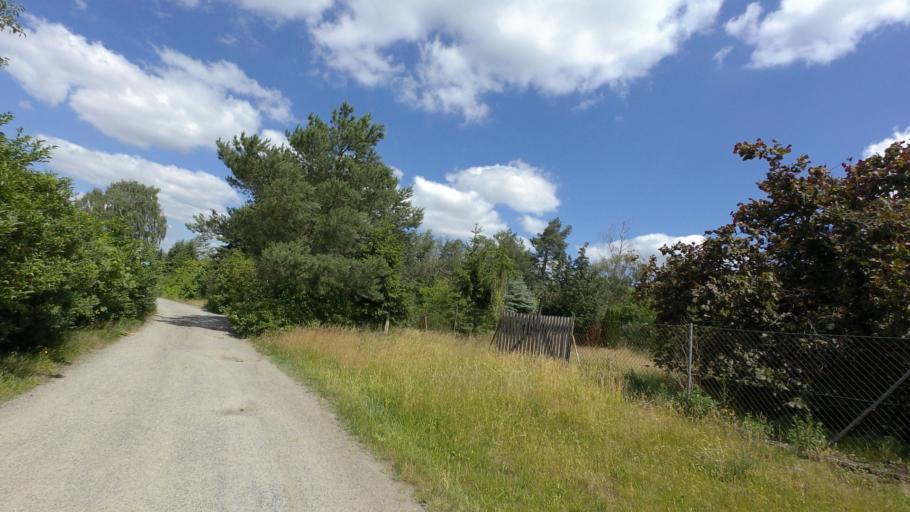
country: DE
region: Brandenburg
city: Finsterwalde
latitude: 51.6447
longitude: 13.6870
